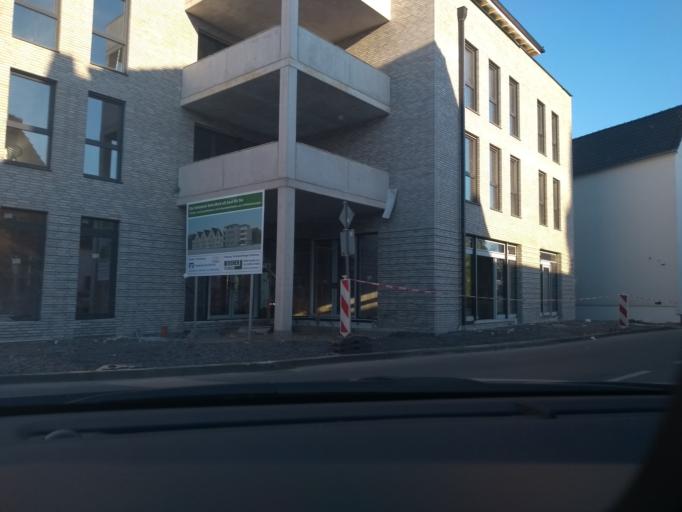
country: DE
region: North Rhine-Westphalia
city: Selm
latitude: 51.6652
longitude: 7.4670
